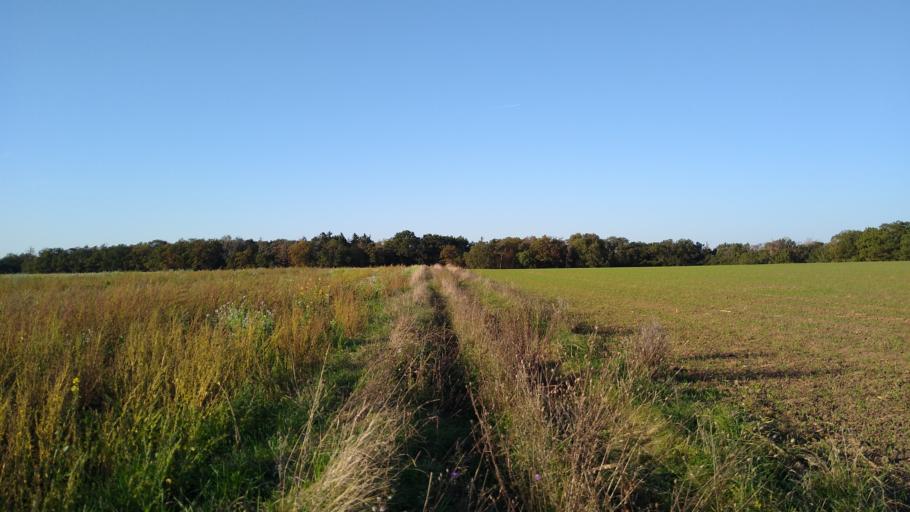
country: DE
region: Bavaria
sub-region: Regierungsbezirk Mittelfranken
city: Obermichelbach
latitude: 49.5003
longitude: 10.9302
